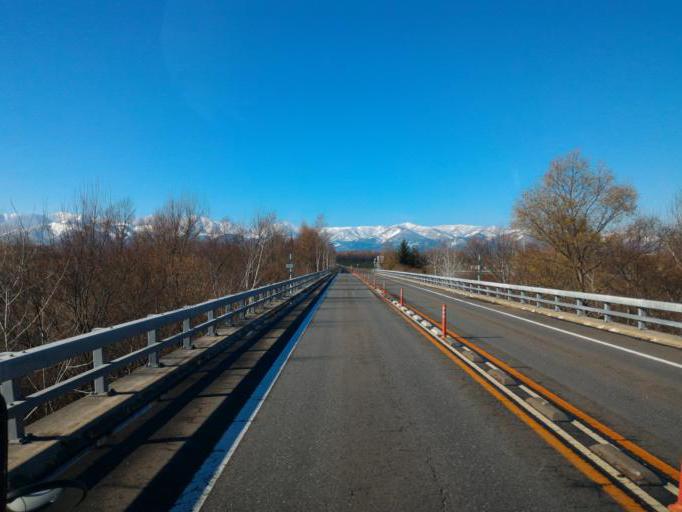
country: JP
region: Hokkaido
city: Otofuke
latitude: 42.9788
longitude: 142.9487
